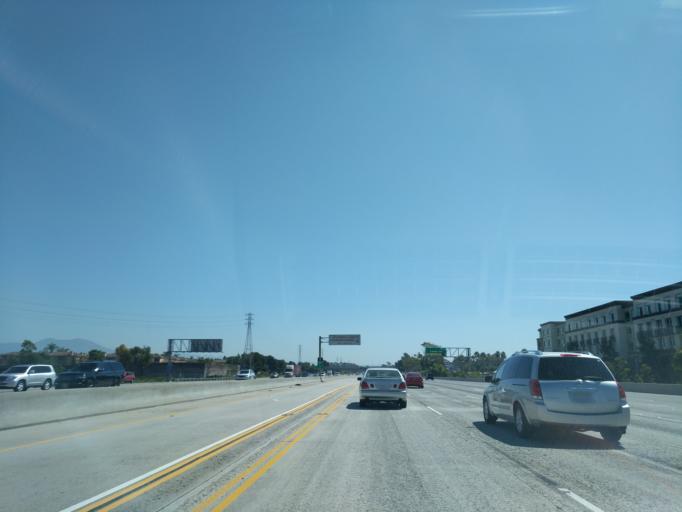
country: US
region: California
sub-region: Orange County
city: Irvine
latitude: 33.6745
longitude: -117.8381
